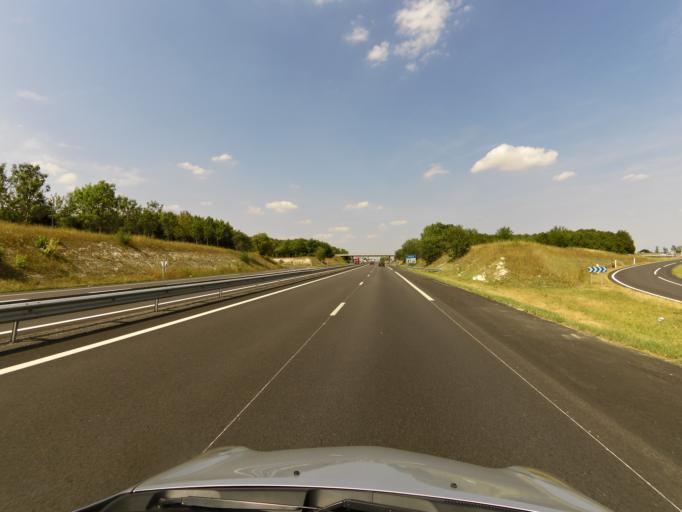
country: FR
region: Picardie
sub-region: Departement de l'Aisne
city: Guignicourt
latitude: 49.4288
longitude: 3.9312
